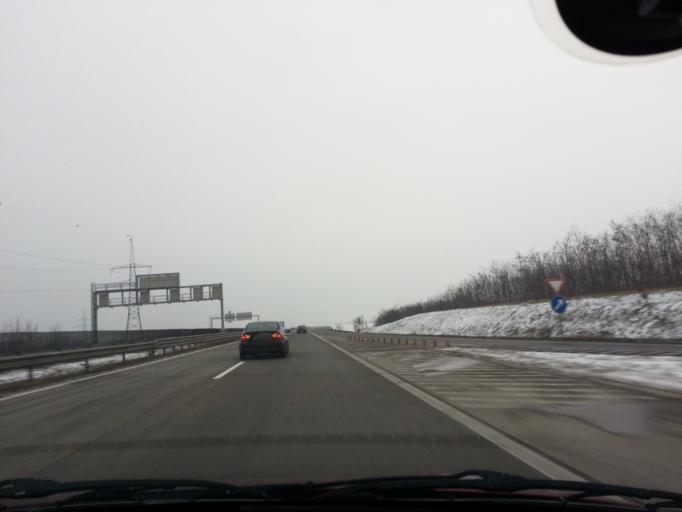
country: HU
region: Pest
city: Ecser
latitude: 47.4615
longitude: 19.3305
